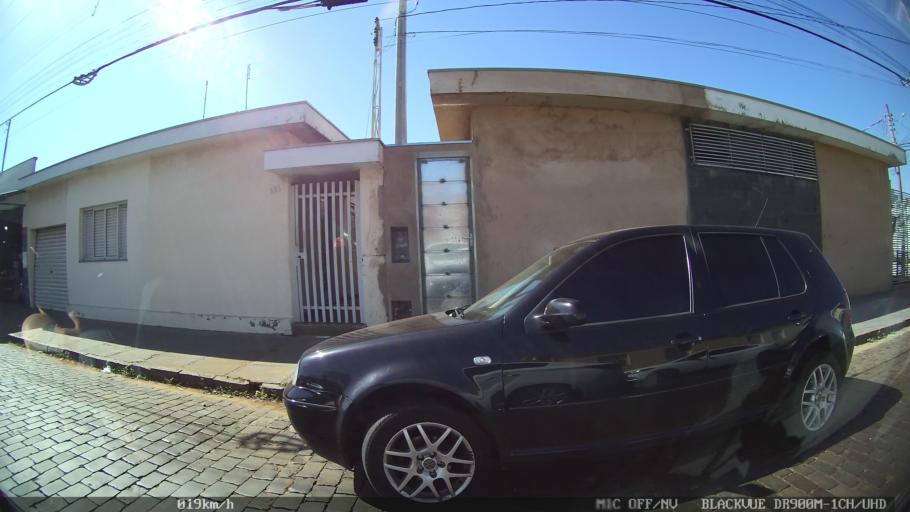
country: BR
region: Sao Paulo
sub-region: Batatais
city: Batatais
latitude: -20.8951
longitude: -47.5836
